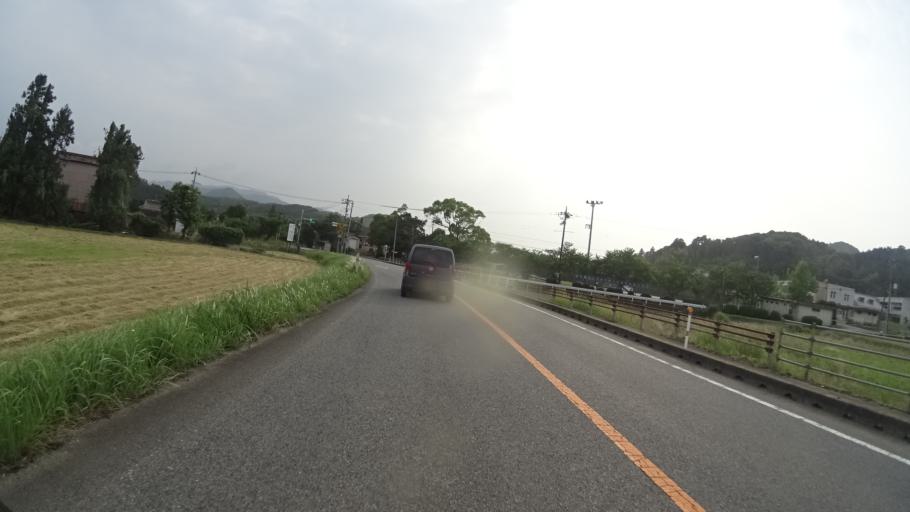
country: JP
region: Yamaguchi
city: Nagato
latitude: 34.2592
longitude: 131.0318
